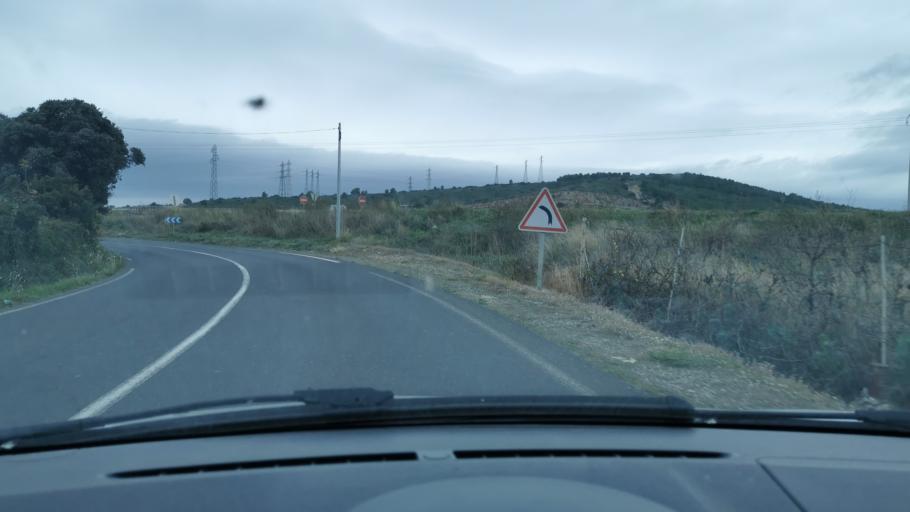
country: FR
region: Languedoc-Roussillon
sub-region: Departement de l'Herault
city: Balaruc-le-Vieux
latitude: 43.4448
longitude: 3.7125
